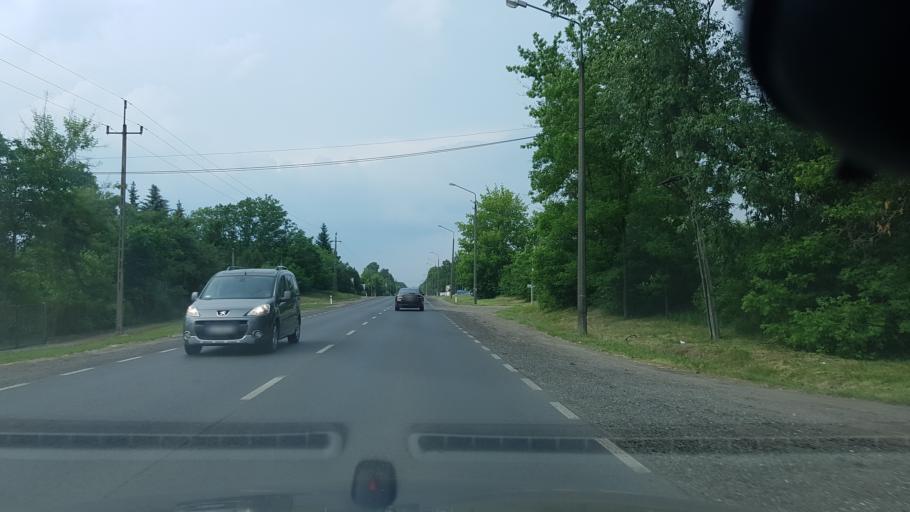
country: PL
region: Masovian Voivodeship
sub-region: Powiat legionowski
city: Michalow-Reginow
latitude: 52.4237
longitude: 20.9745
